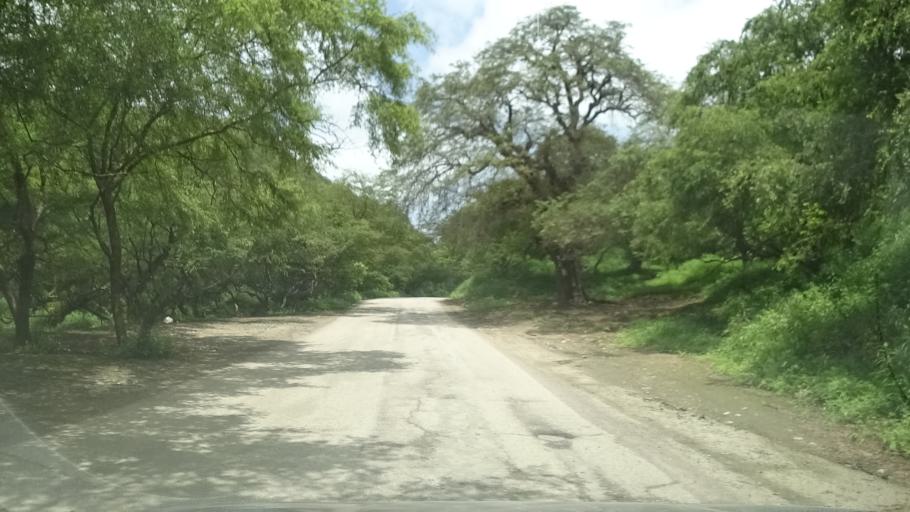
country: OM
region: Zufar
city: Salalah
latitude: 17.1716
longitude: 54.1668
